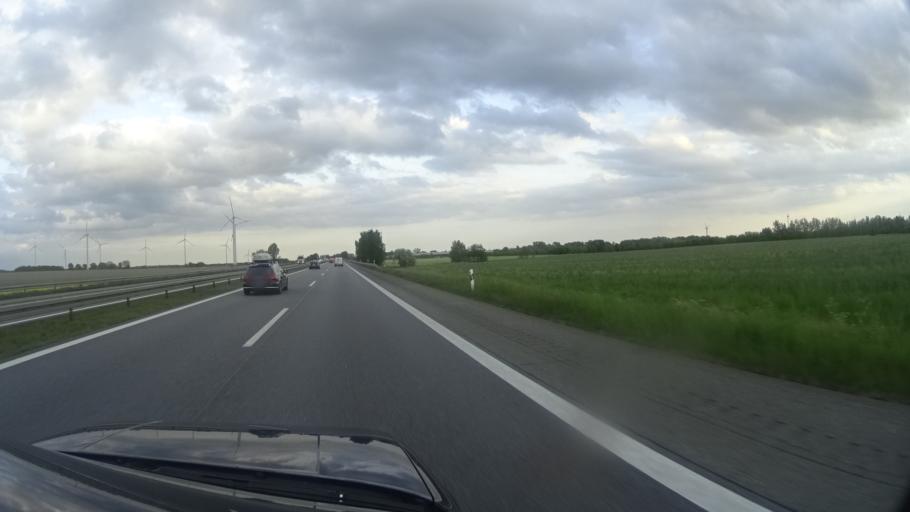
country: DE
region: Brandenburg
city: Dabergotz
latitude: 52.9205
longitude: 12.7169
